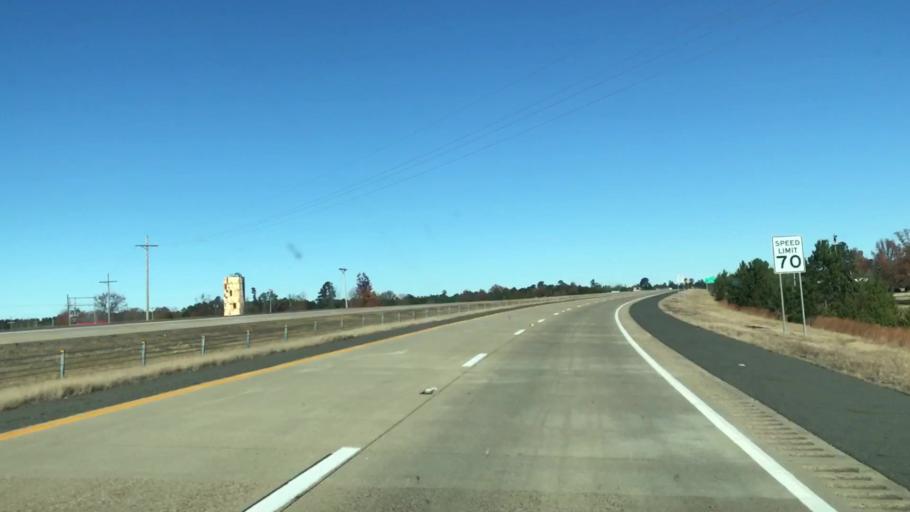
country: US
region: Texas
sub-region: Bowie County
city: Texarkana
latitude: 33.2542
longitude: -93.8931
